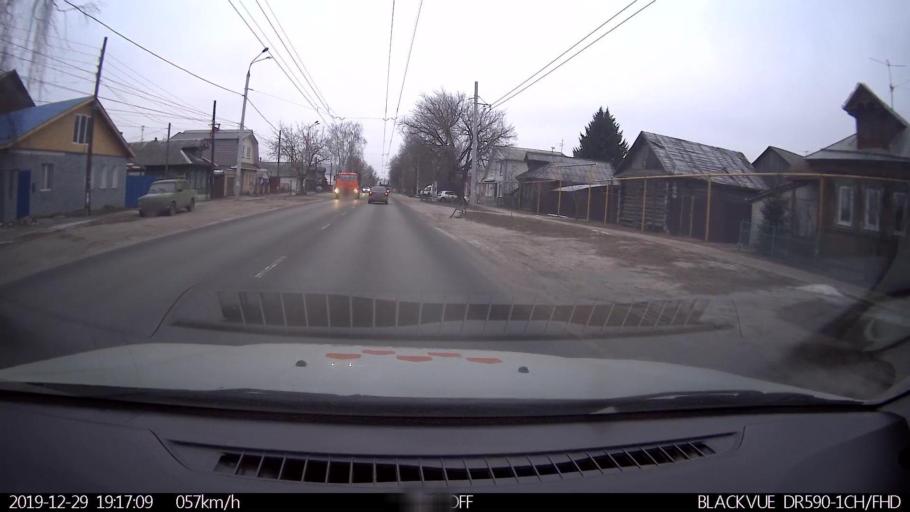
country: RU
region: Nizjnij Novgorod
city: Gorbatovka
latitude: 56.3801
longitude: 43.8203
